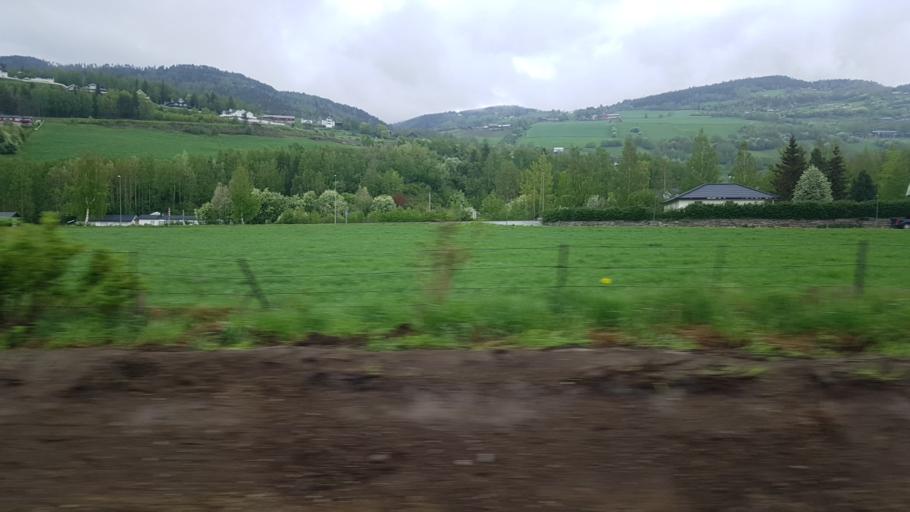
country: NO
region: Oppland
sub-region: Nord-Fron
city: Vinstra
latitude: 61.5792
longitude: 9.7660
